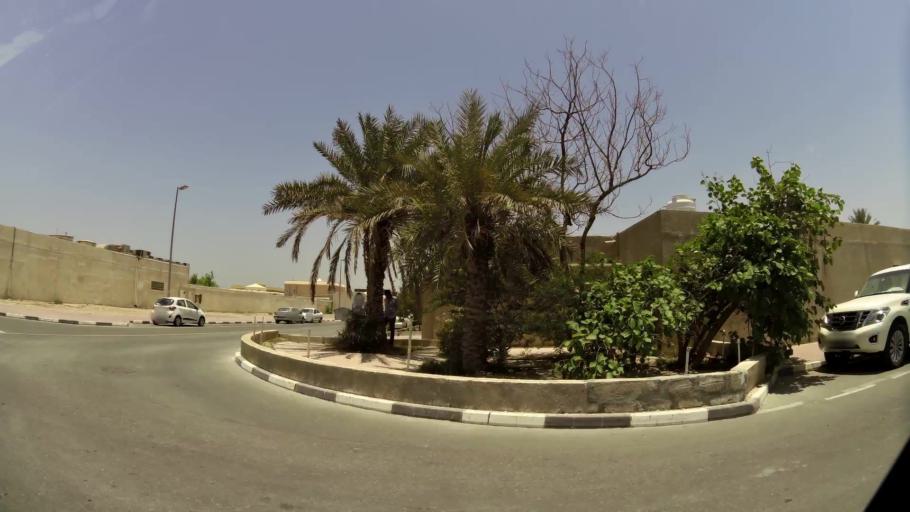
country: AE
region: Ash Shariqah
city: Sharjah
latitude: 25.2327
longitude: 55.2846
